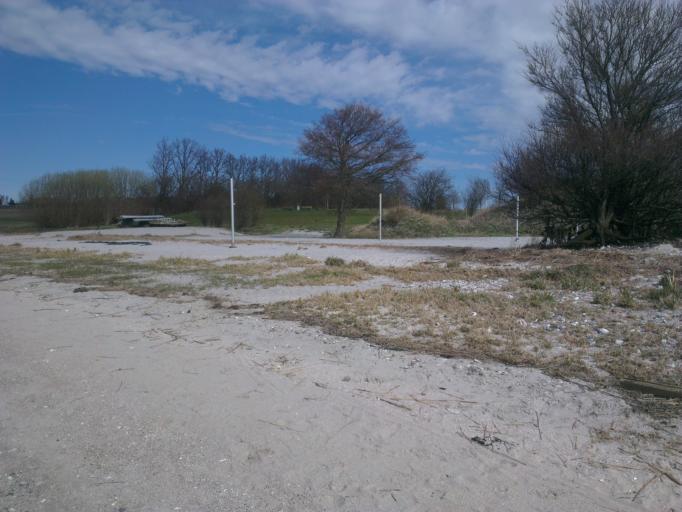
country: DK
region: Capital Region
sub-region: Frederikssund Kommune
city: Frederikssund
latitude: 55.8190
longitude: 12.0656
